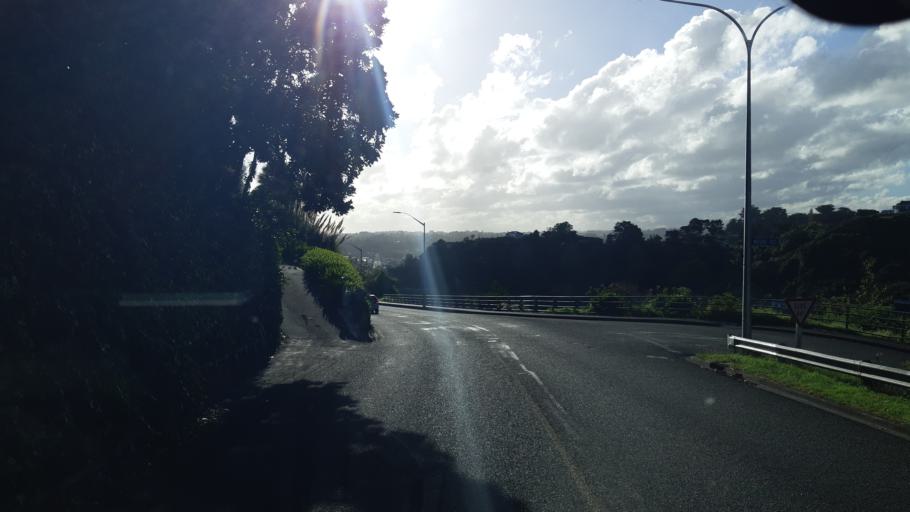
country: NZ
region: Manawatu-Wanganui
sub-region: Wanganui District
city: Wanganui
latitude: -39.9360
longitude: 175.0665
